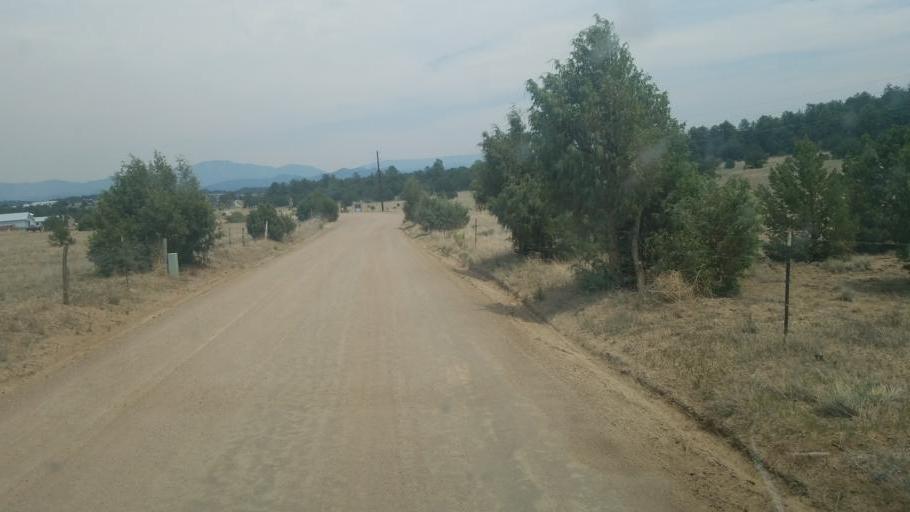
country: US
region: Colorado
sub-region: Custer County
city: Westcliffe
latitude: 38.2993
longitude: -105.4880
